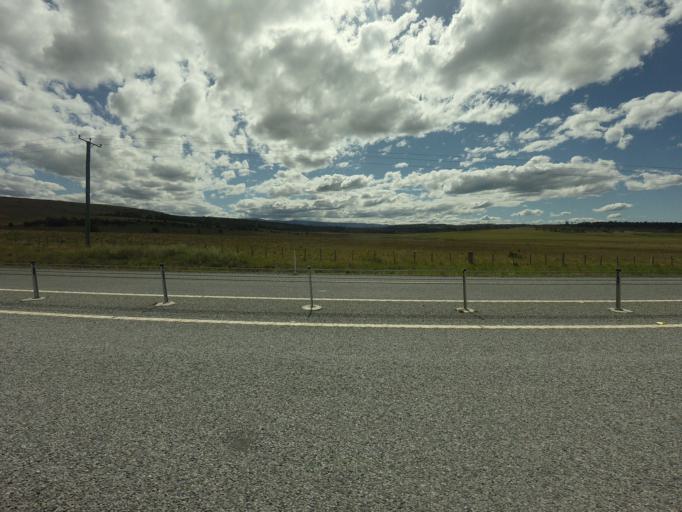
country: AU
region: Tasmania
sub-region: Northern Midlands
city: Evandale
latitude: -42.0997
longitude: 147.4523
